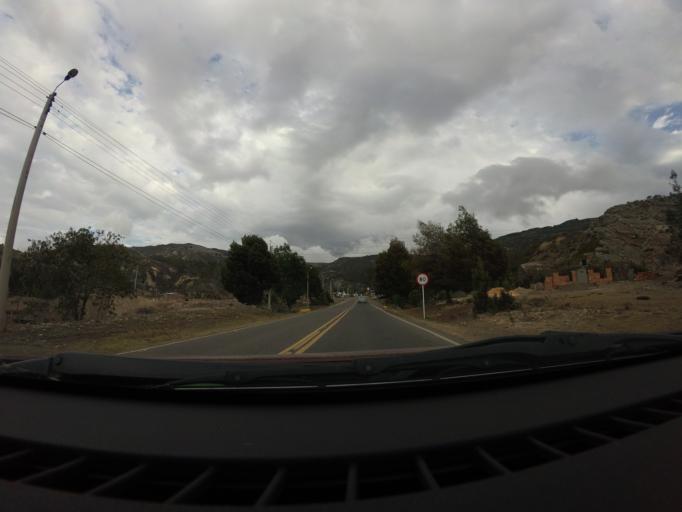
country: CO
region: Boyaca
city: Cucaita
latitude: 5.5397
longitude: -73.4525
